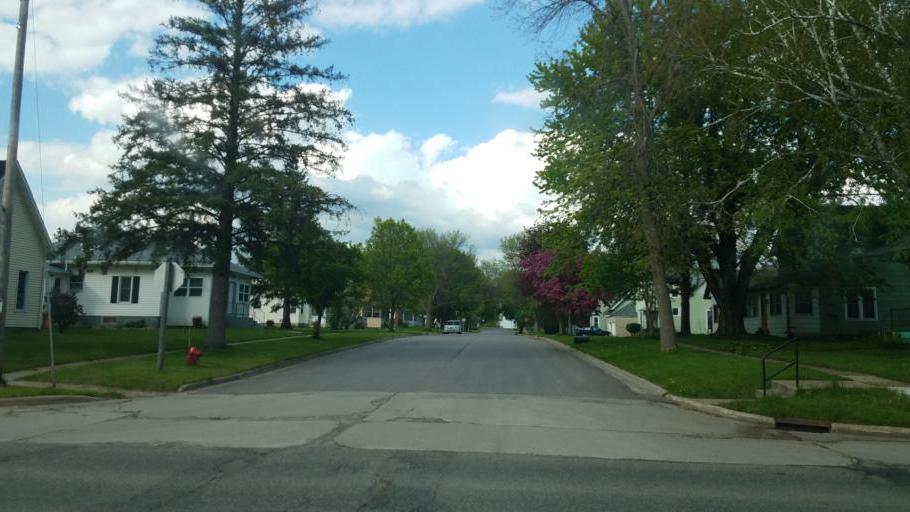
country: US
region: Wisconsin
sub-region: Vernon County
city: Hillsboro
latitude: 43.6508
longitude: -90.3448
